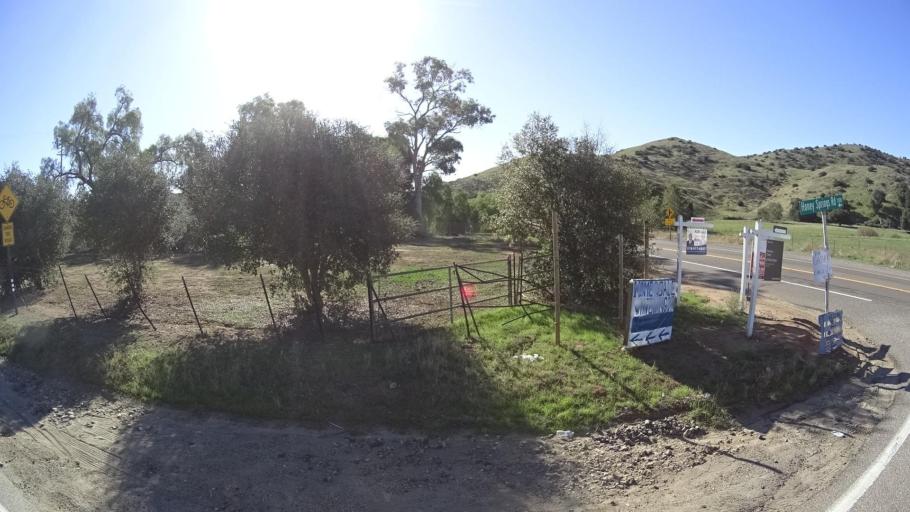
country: US
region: California
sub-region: San Diego County
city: Jamul
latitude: 32.6700
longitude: -116.8252
